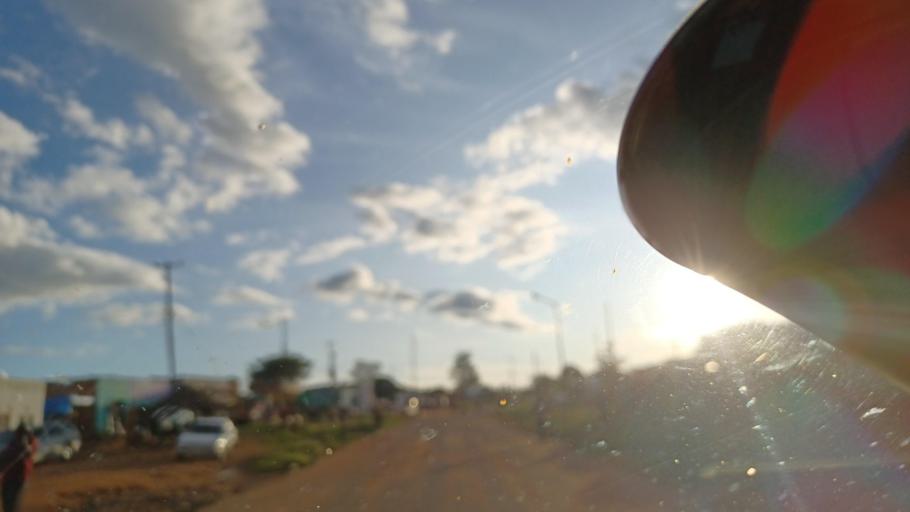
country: ZM
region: North-Western
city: Kasempa
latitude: -13.4589
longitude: 25.8404
